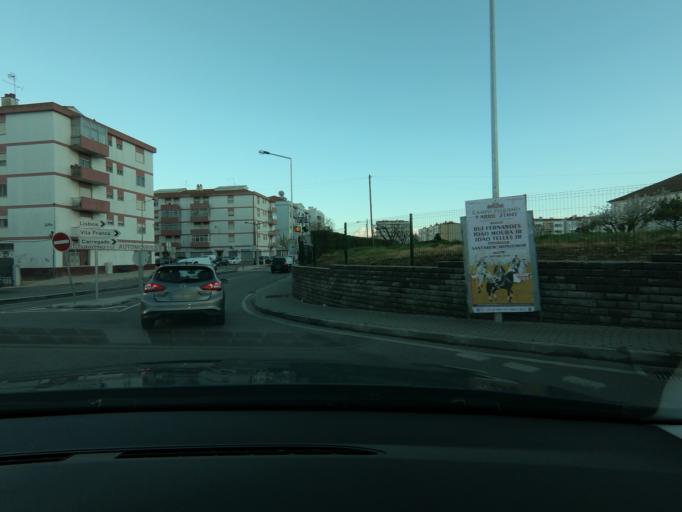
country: PT
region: Lisbon
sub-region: Alenquer
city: Carregado
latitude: 39.0262
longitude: -8.9801
